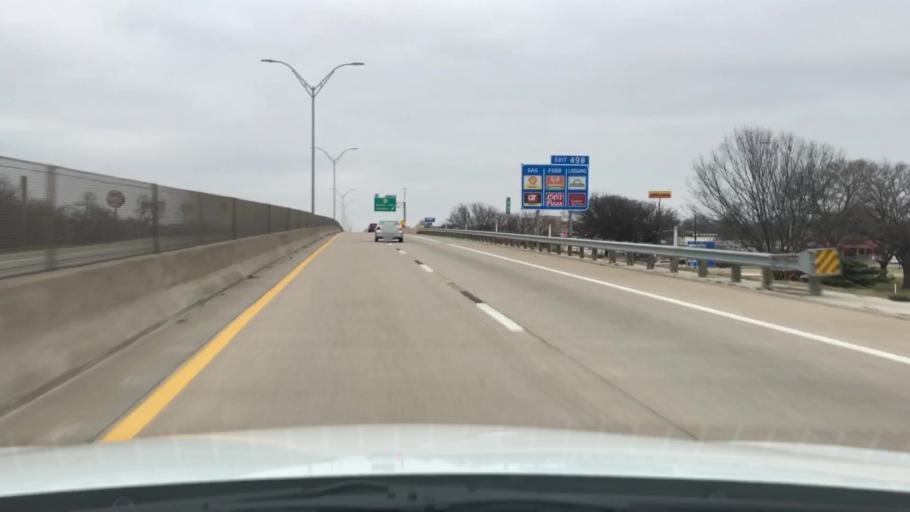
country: US
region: Texas
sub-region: Cooke County
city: Gainesville
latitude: 33.6231
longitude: -97.1516
